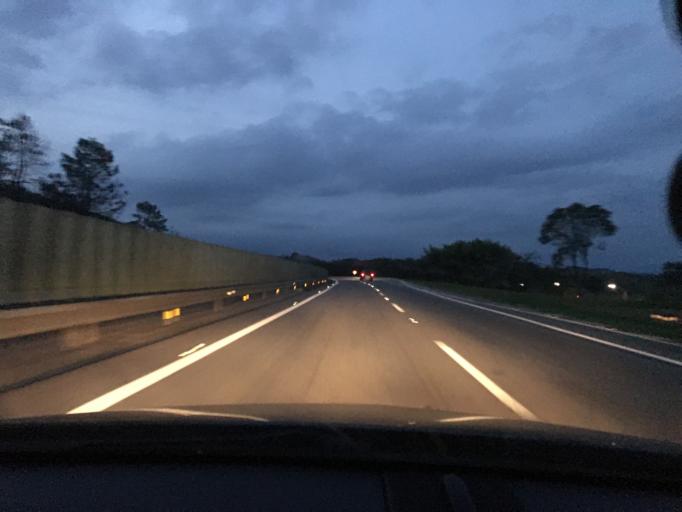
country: BR
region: Sao Paulo
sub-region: Santa Isabel
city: Santa Isabel
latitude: -23.3435
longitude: -46.1272
